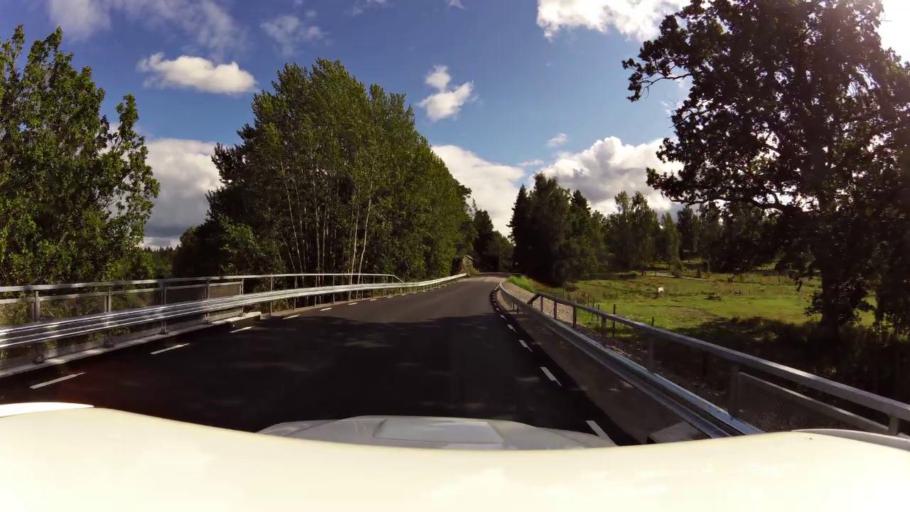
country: SE
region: OEstergoetland
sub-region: Kinda Kommun
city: Rimforsa
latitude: 58.2279
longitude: 15.7022
